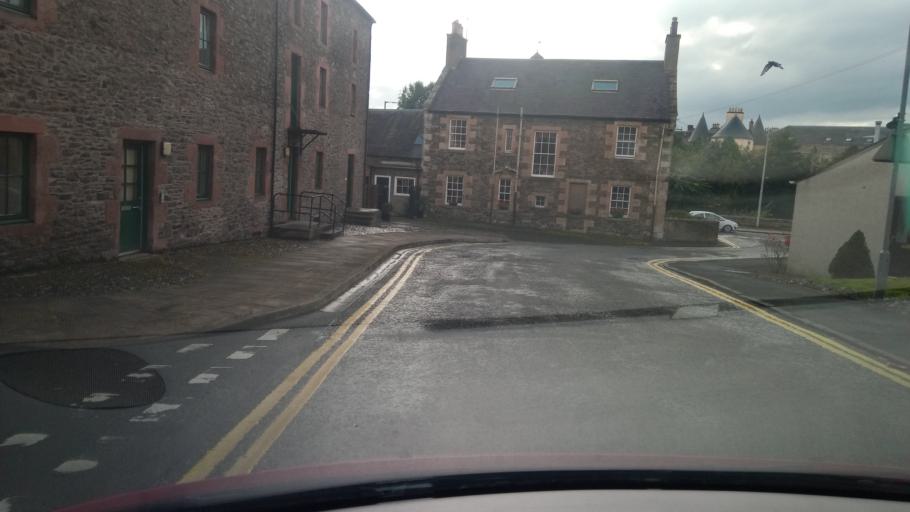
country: GB
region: Scotland
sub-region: The Scottish Borders
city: Hawick
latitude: 55.4206
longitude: -2.7859
